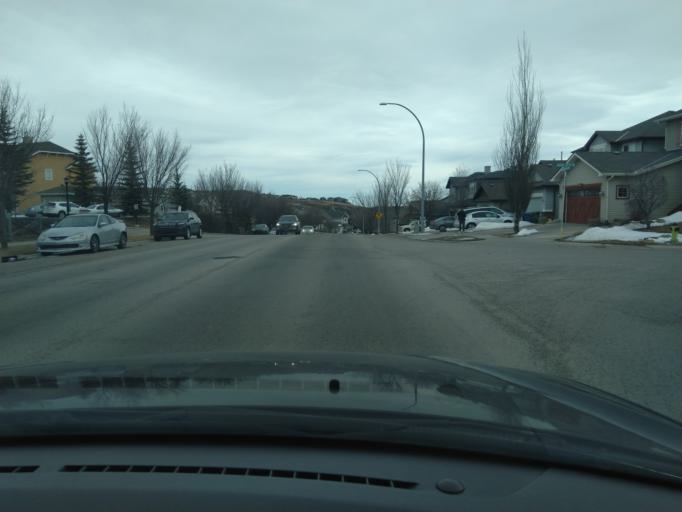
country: CA
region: Alberta
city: Calgary
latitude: 51.1615
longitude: -114.1020
